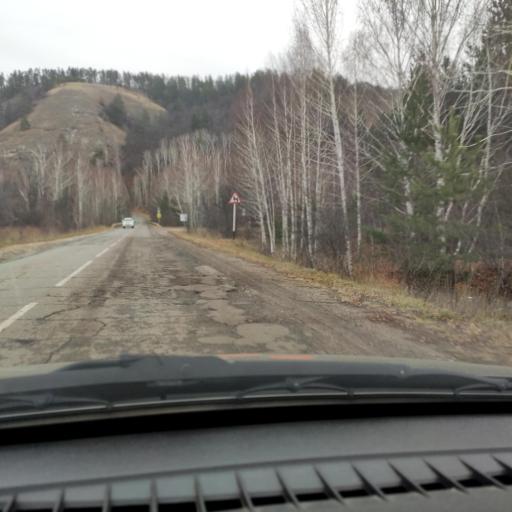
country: RU
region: Samara
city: Zhigulevsk
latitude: 53.4309
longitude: 49.6693
